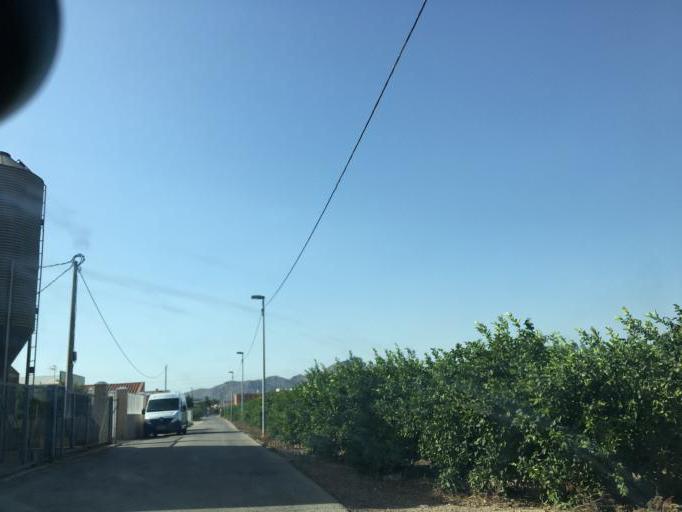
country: ES
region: Murcia
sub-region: Murcia
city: Santomera
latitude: 38.0306
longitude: -1.0573
